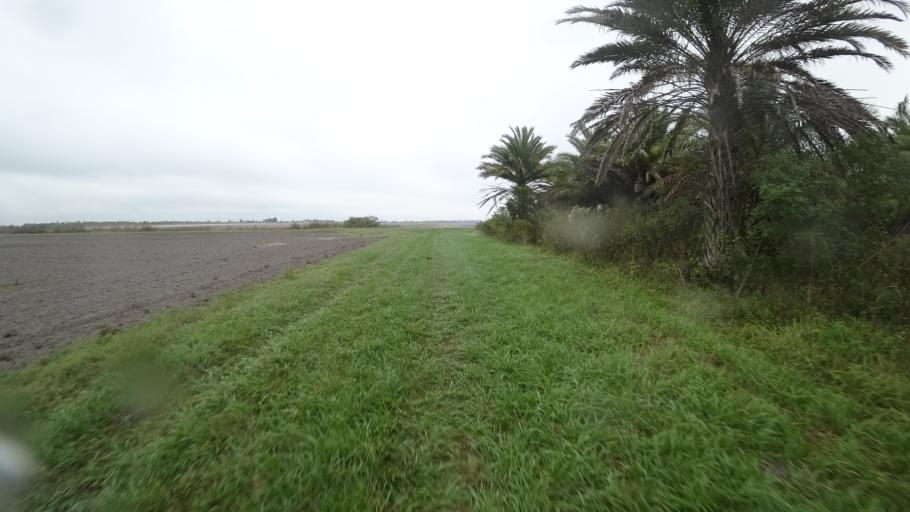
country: US
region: Florida
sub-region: Sarasota County
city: Warm Mineral Springs
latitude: 27.2844
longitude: -82.1754
